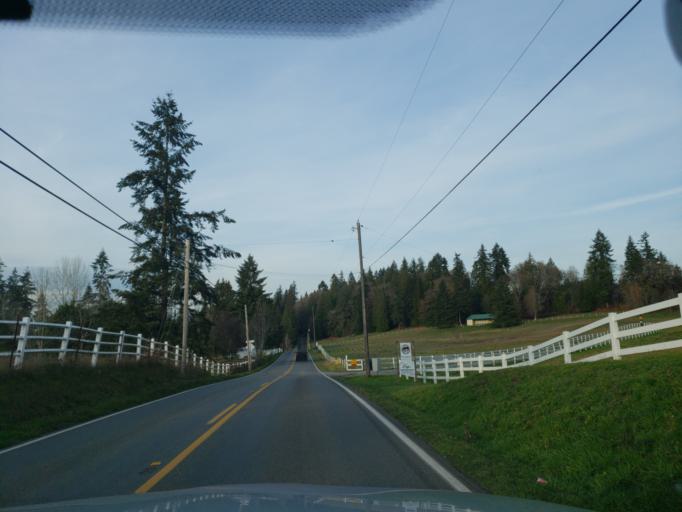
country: US
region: Washington
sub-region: Snohomish County
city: Cathcart
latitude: 47.8343
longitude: -122.0774
